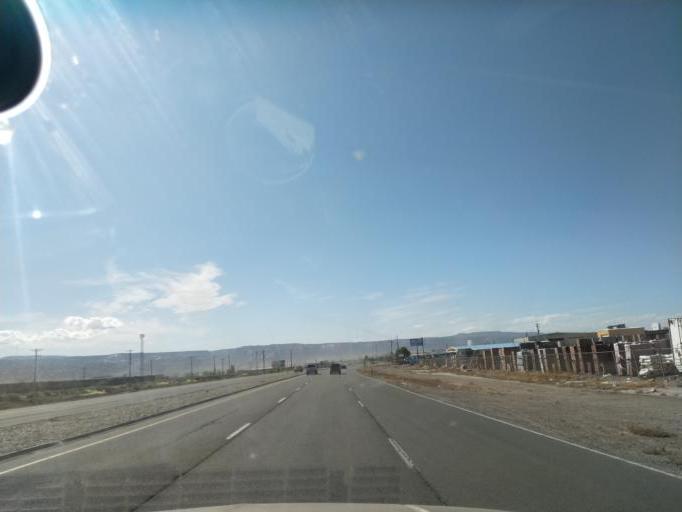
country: US
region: Colorado
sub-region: Mesa County
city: Fruitvale
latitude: 39.0719
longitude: -108.5211
